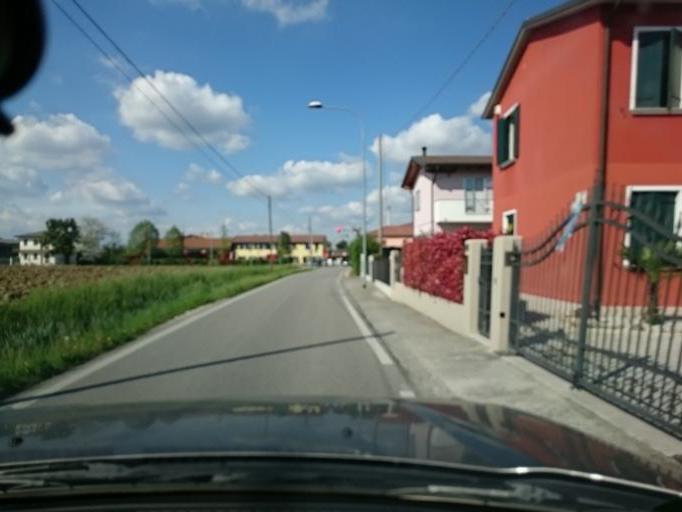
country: IT
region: Veneto
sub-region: Provincia di Padova
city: Pionca
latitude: 45.4618
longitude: 11.9765
